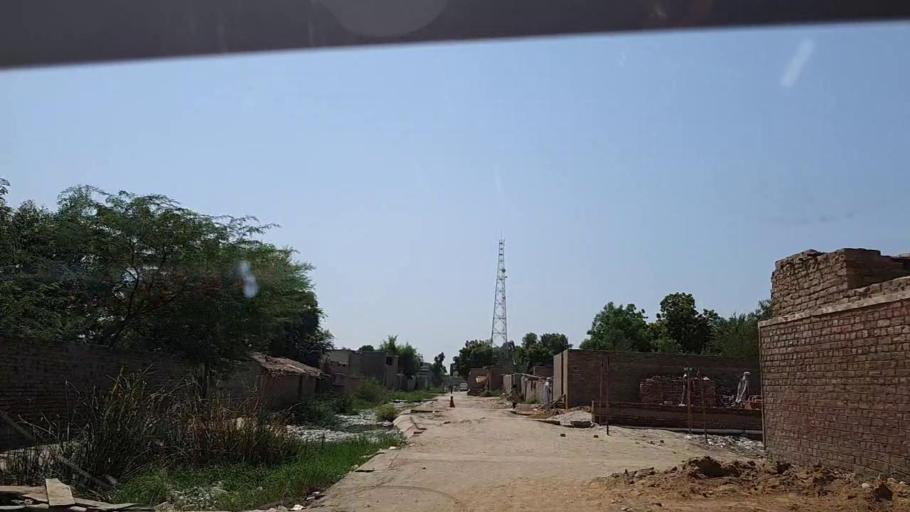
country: PK
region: Sindh
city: Ghauspur
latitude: 28.1386
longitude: 69.0879
